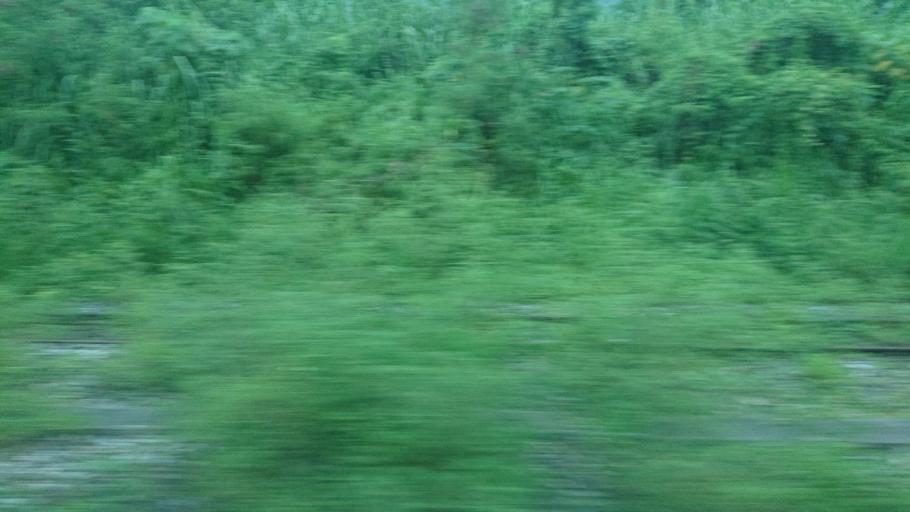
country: TW
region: Taiwan
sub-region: Hualien
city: Hualian
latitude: 24.1236
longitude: 121.6382
